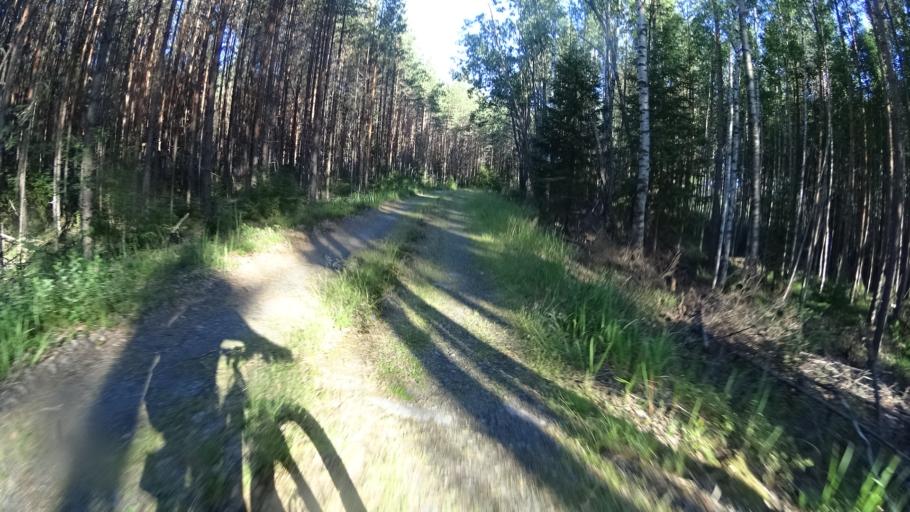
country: FI
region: Uusimaa
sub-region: Helsinki
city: Karkkila
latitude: 60.6624
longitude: 24.1333
